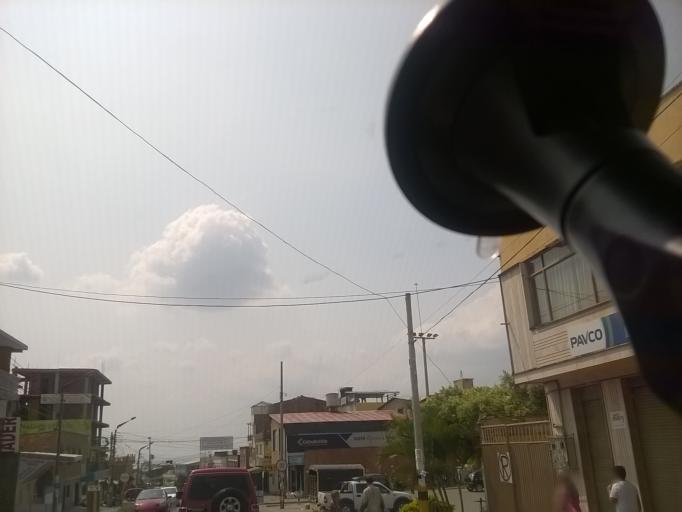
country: CO
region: Cundinamarca
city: San Antonio del Tequendama
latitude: 4.6294
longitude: -74.4639
